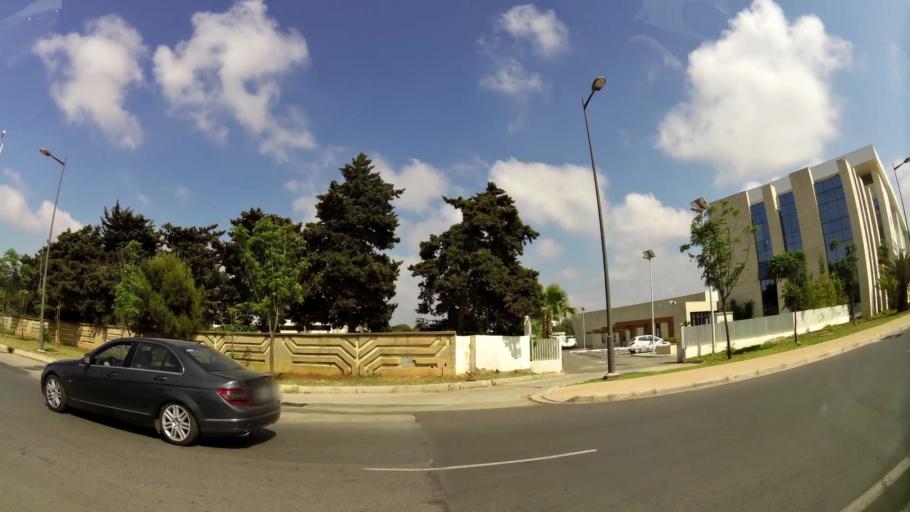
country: MA
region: Rabat-Sale-Zemmour-Zaer
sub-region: Rabat
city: Rabat
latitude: 33.9747
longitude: -6.8707
